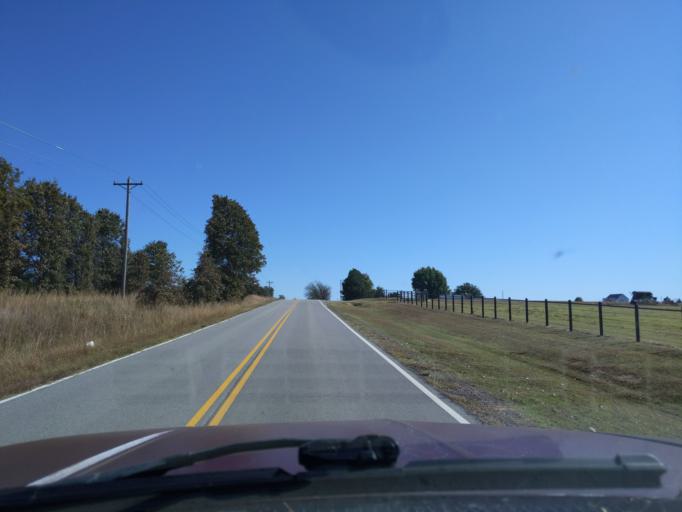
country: US
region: Oklahoma
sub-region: Creek County
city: Bristow
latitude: 35.7119
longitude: -96.4003
